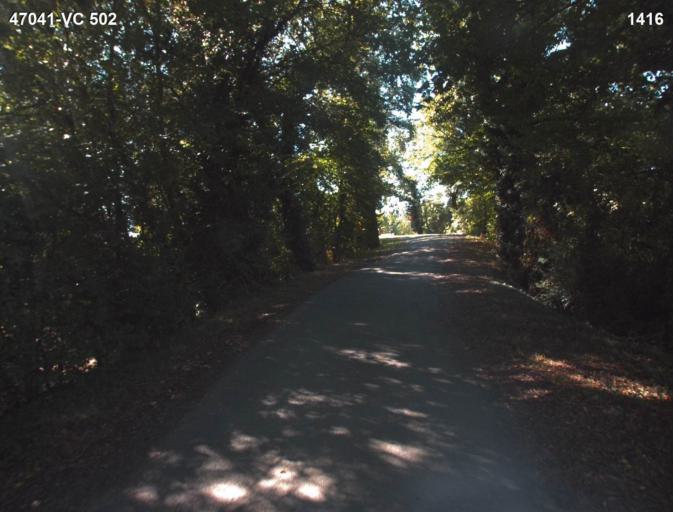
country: FR
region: Aquitaine
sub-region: Departement du Lot-et-Garonne
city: Port-Sainte-Marie
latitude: 44.2199
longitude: 0.3917
